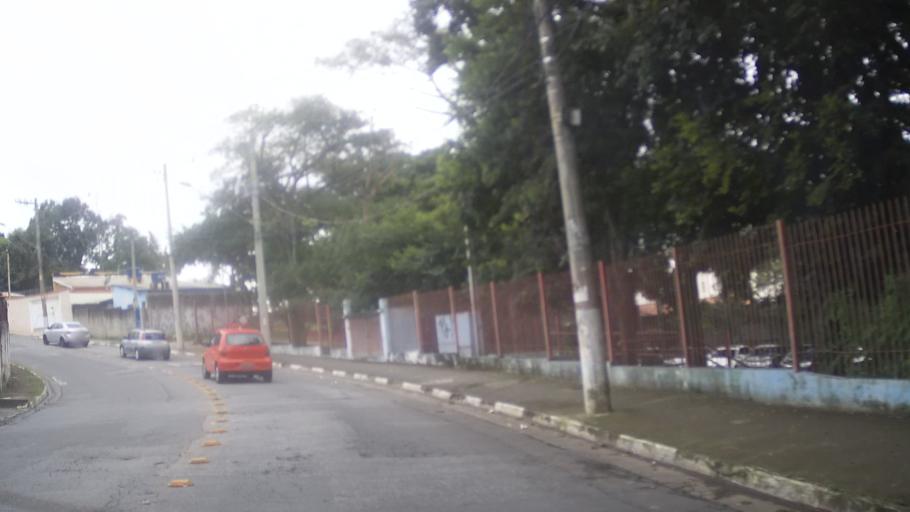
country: BR
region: Sao Paulo
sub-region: Guarulhos
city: Guarulhos
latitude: -23.4496
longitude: -46.5256
